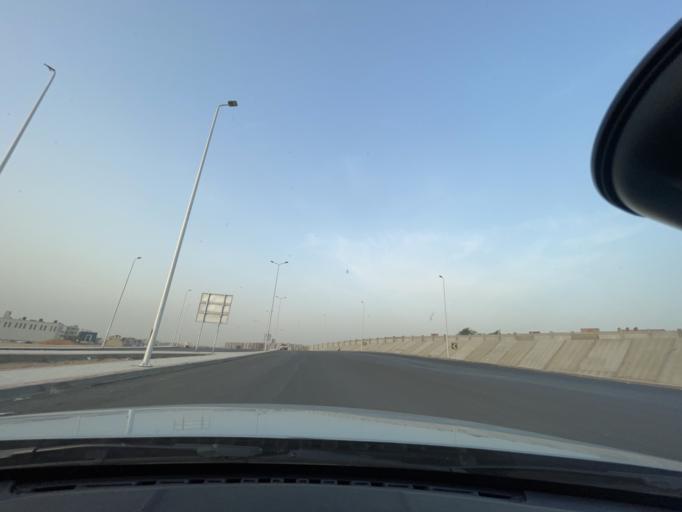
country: EG
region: Muhafazat al Qahirah
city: Cairo
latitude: 30.0237
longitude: 31.3449
